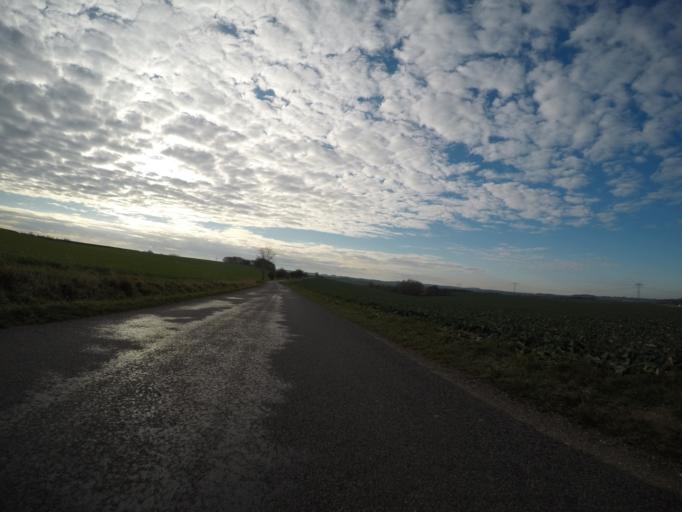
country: DE
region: Thuringia
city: Vollmershain
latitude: 50.8594
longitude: 12.3002
